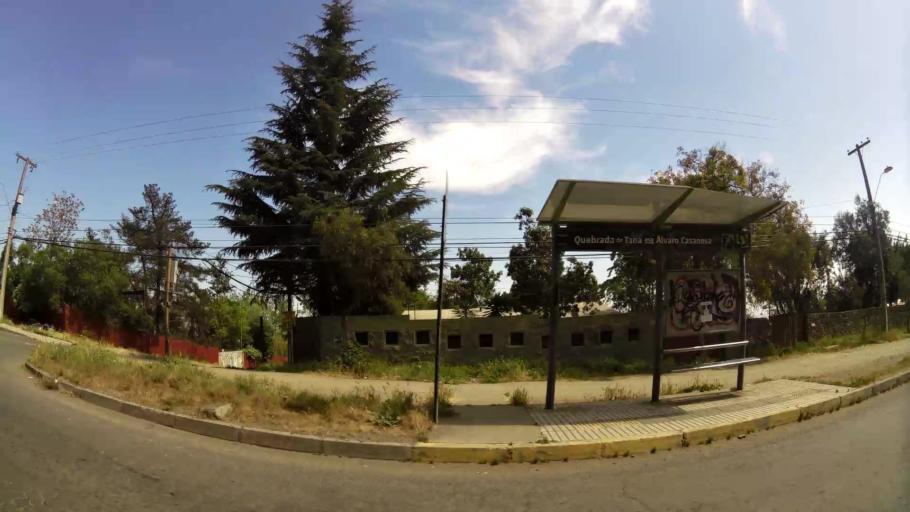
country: CL
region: Santiago Metropolitan
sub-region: Provincia de Santiago
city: Villa Presidente Frei, Nunoa, Santiago, Chile
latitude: -33.4721
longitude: -70.5243
